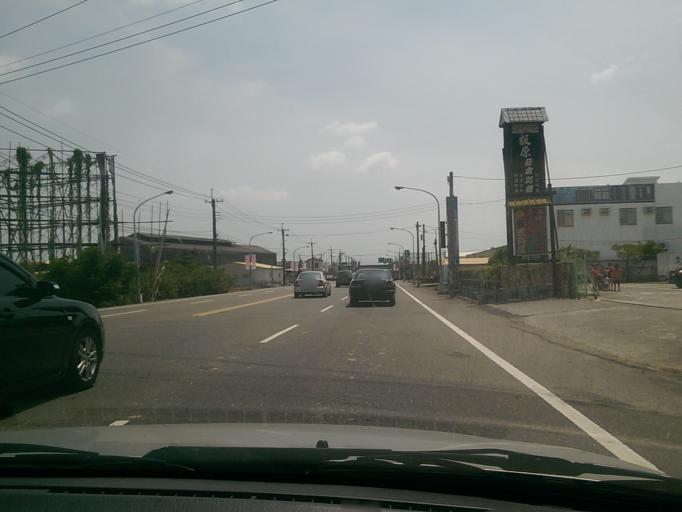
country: TW
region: Taiwan
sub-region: Yunlin
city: Douliu
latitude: 23.6937
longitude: 120.4195
